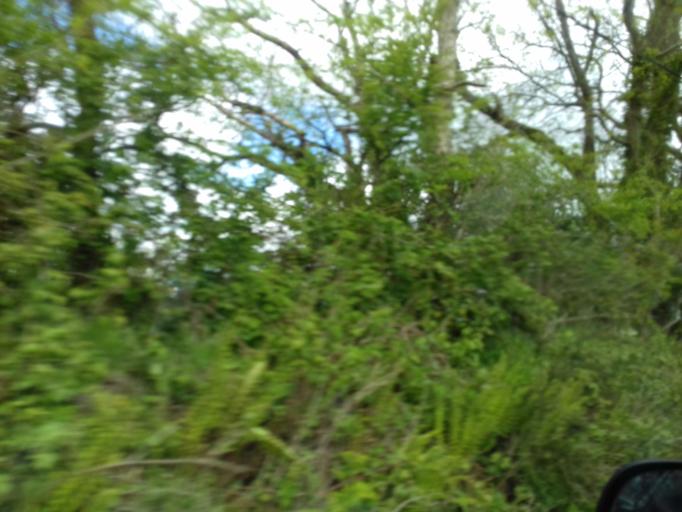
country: IE
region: Leinster
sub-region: Loch Garman
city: Castlebridge
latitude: 52.3808
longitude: -6.5027
